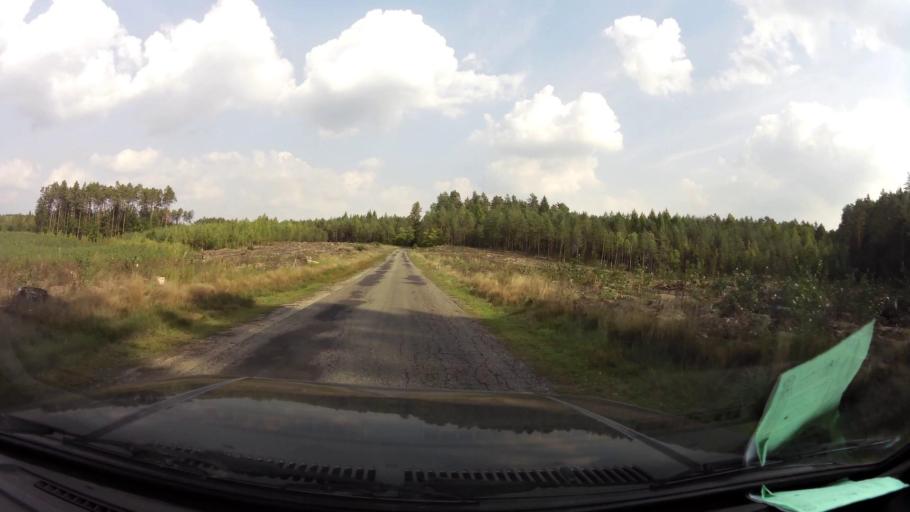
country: PL
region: West Pomeranian Voivodeship
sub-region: Powiat koszalinski
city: Bobolice
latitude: 54.0840
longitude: 16.4773
